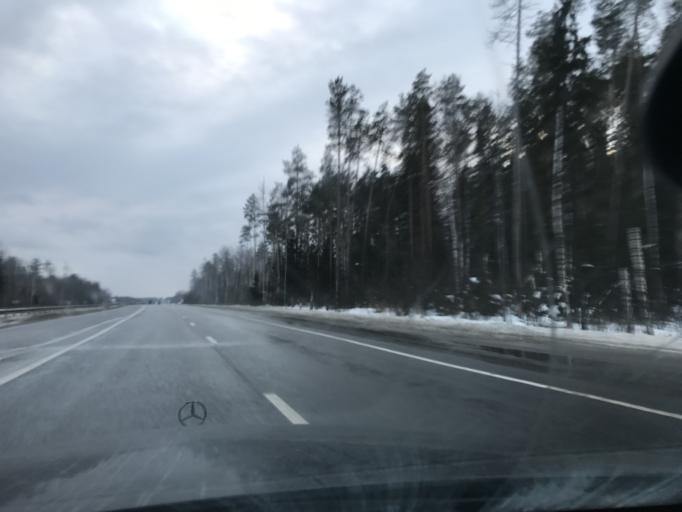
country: RU
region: Vladimir
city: Sudogda
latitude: 56.1389
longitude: 40.8945
